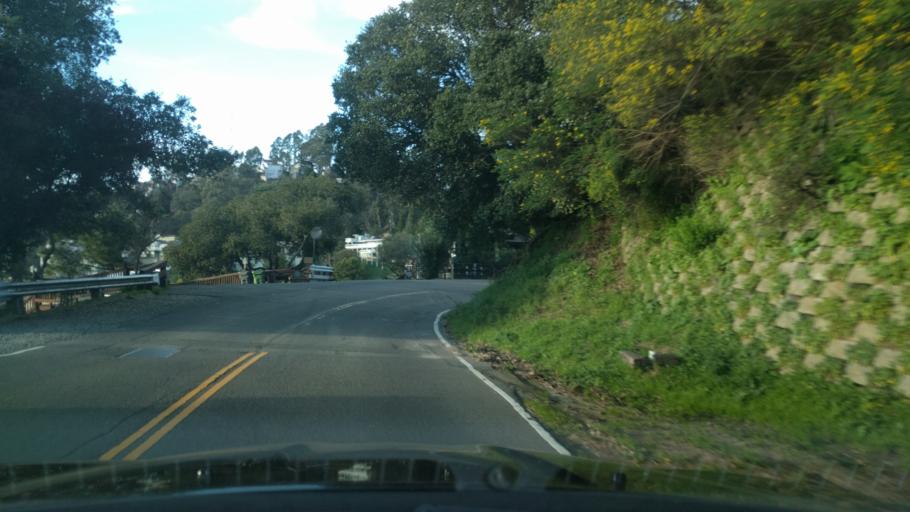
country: US
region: California
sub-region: Alameda County
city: Piedmont
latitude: 37.8422
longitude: -122.1979
